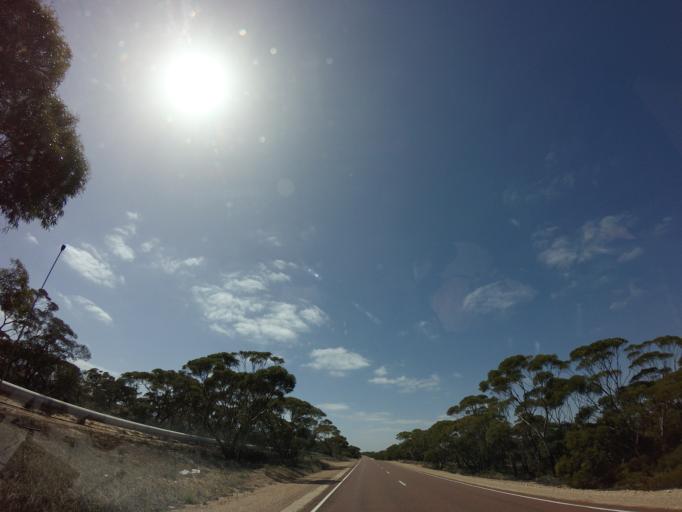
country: AU
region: South Australia
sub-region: Kimba
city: Caralue
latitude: -33.1036
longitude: 135.5241
